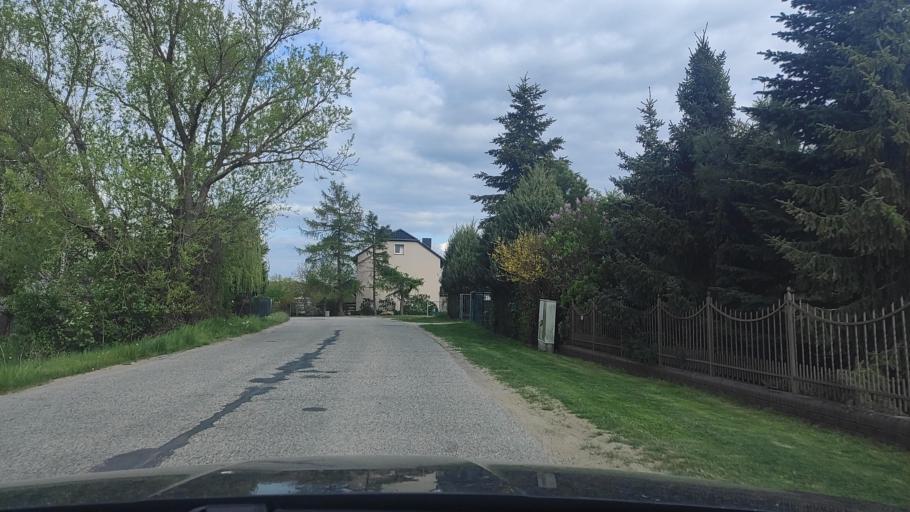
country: PL
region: Greater Poland Voivodeship
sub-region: Powiat poznanski
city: Pobiedziska
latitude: 52.4520
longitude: 17.2403
